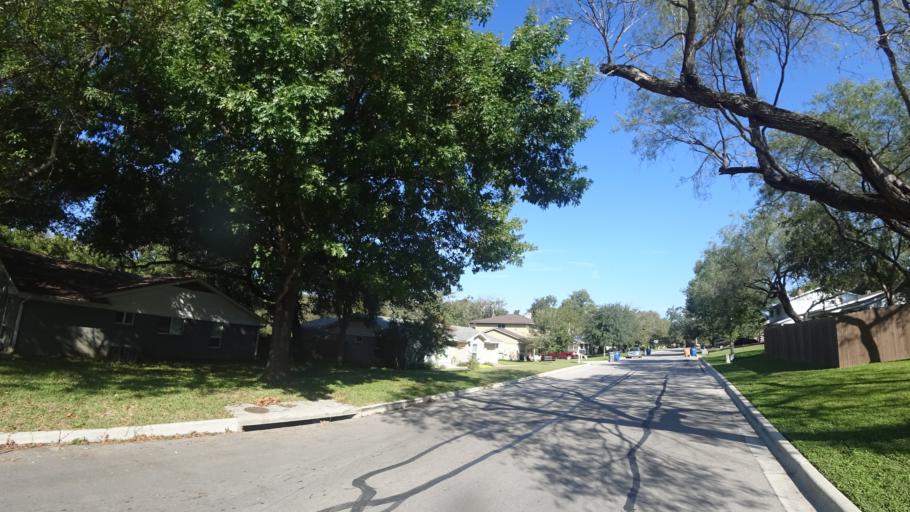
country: US
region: Texas
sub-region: Travis County
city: Austin
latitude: 30.3190
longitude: -97.6708
